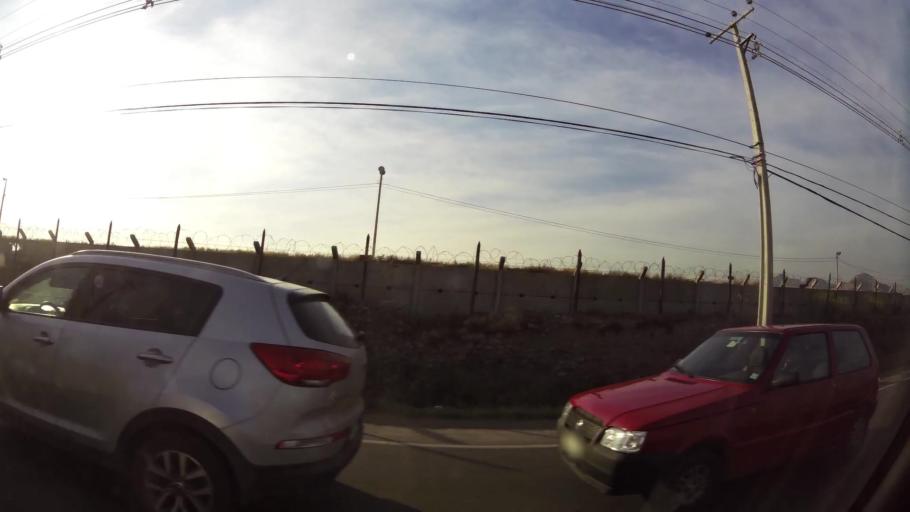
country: CL
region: Santiago Metropolitan
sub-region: Provincia de Maipo
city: San Bernardo
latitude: -33.5491
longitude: -70.7480
